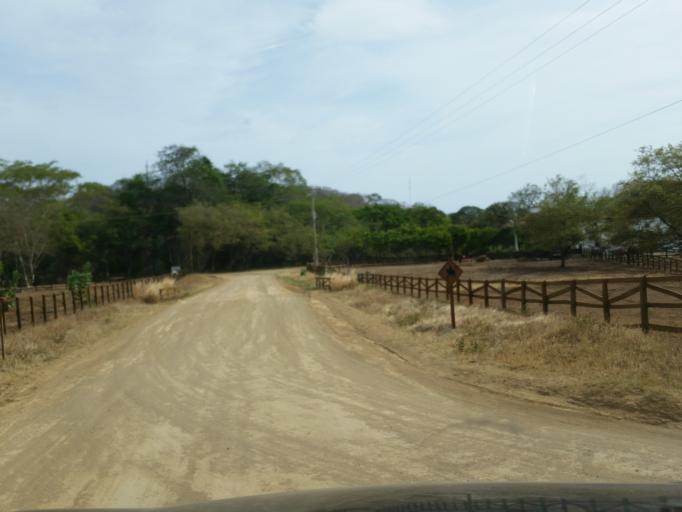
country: NI
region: Rivas
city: Tola
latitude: 11.4435
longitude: -86.0811
